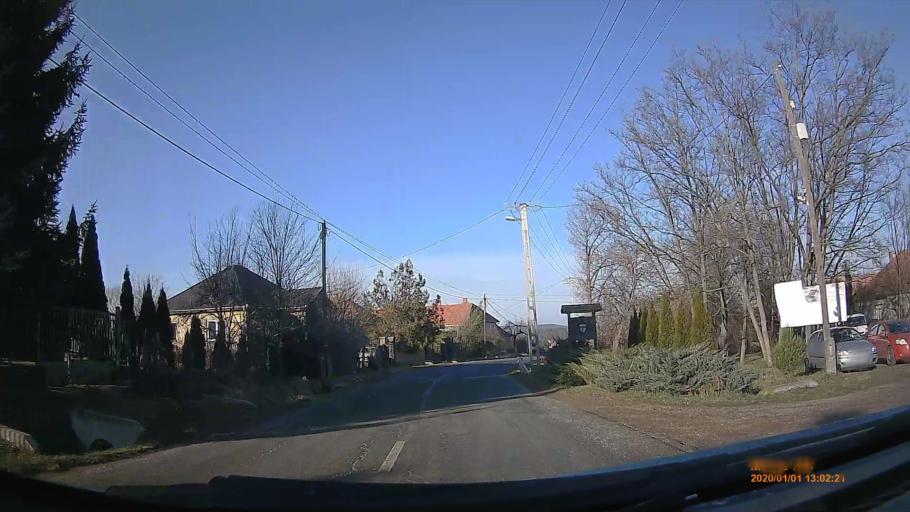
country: HU
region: Heves
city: Parad
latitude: 47.9351
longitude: 20.0246
